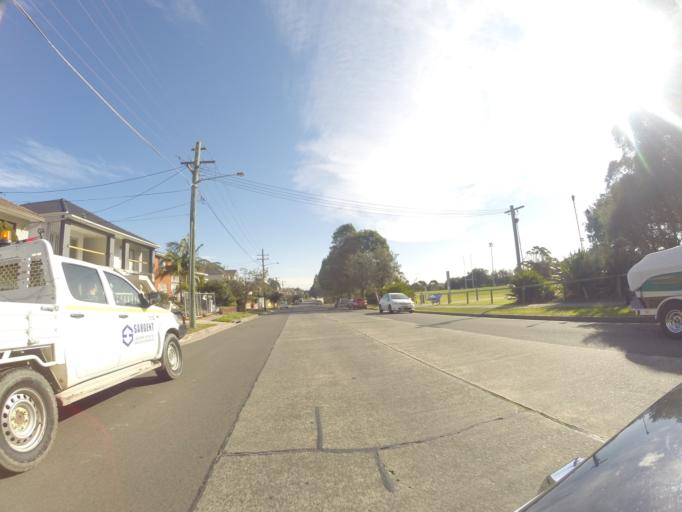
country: AU
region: New South Wales
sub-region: Randwick
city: South Coogee
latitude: -33.9362
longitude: 151.2513
